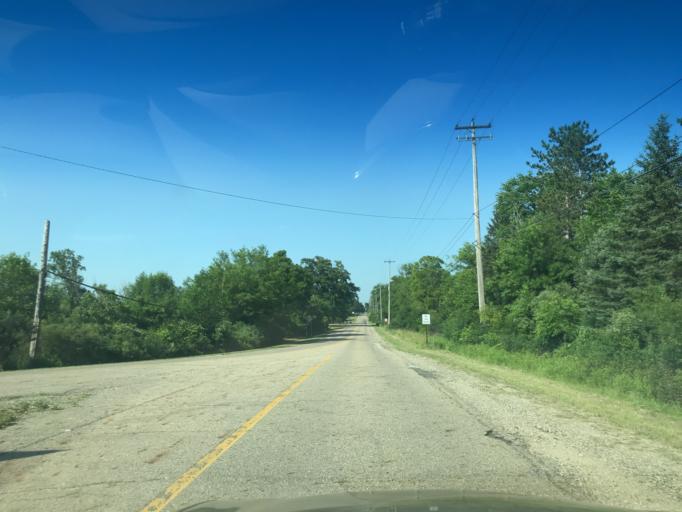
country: US
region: Michigan
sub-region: Eaton County
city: Dimondale
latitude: 42.6884
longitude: -84.6373
